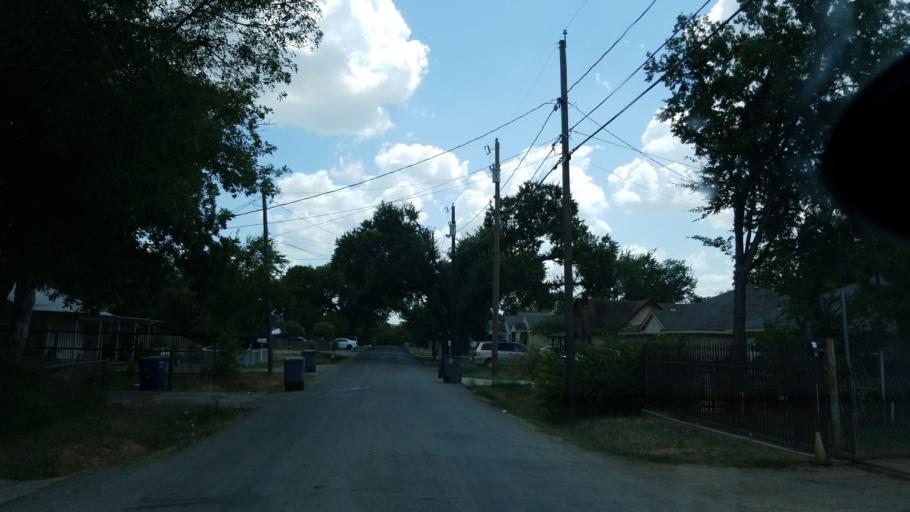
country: US
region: Texas
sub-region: Dallas County
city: Cockrell Hill
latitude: 32.7518
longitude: -96.9140
